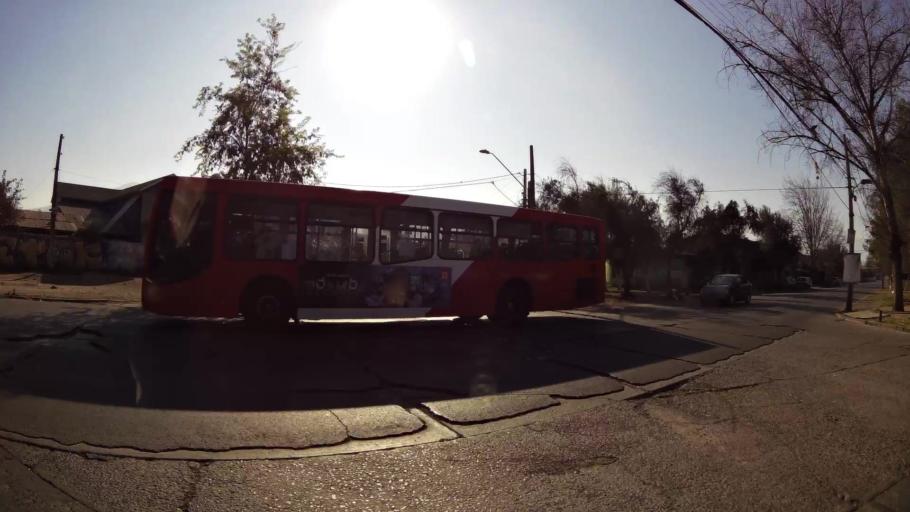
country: CL
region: Santiago Metropolitan
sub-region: Provincia de Santiago
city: Santiago
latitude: -33.3803
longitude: -70.6711
